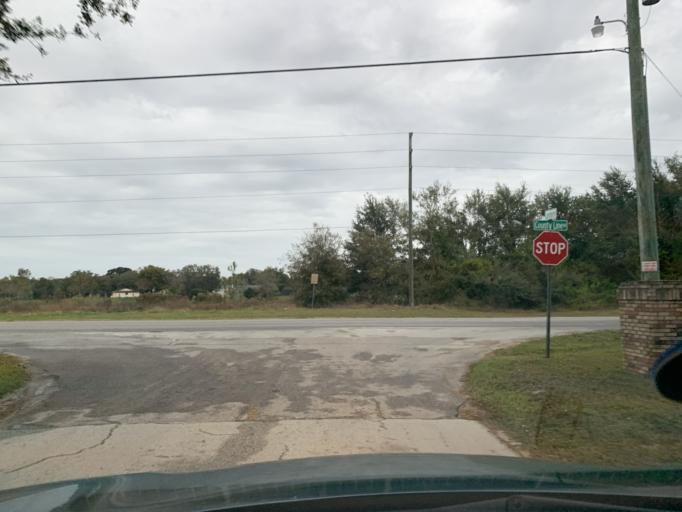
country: US
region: Florida
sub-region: Hernando County
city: Timber Pines
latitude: 28.4337
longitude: -82.5911
